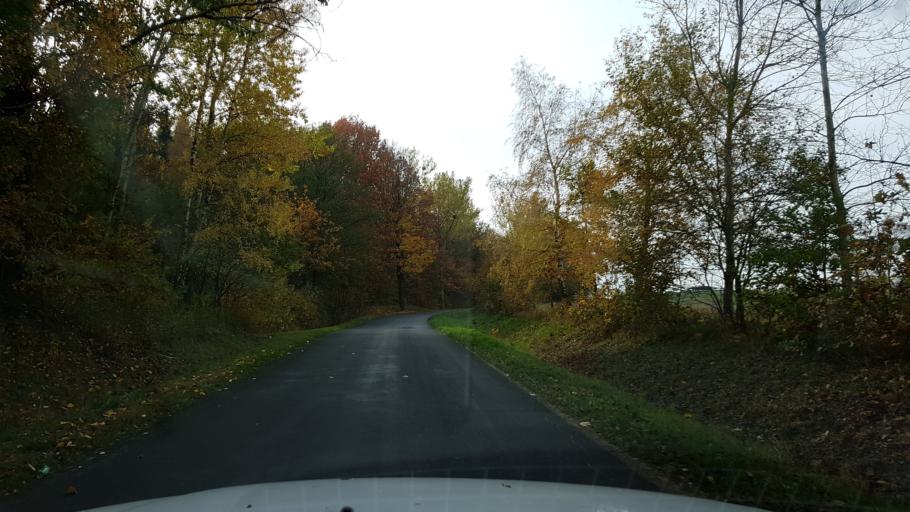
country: PL
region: West Pomeranian Voivodeship
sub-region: Powiat swidwinski
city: Polczyn-Zdroj
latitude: 53.7489
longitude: 16.0486
